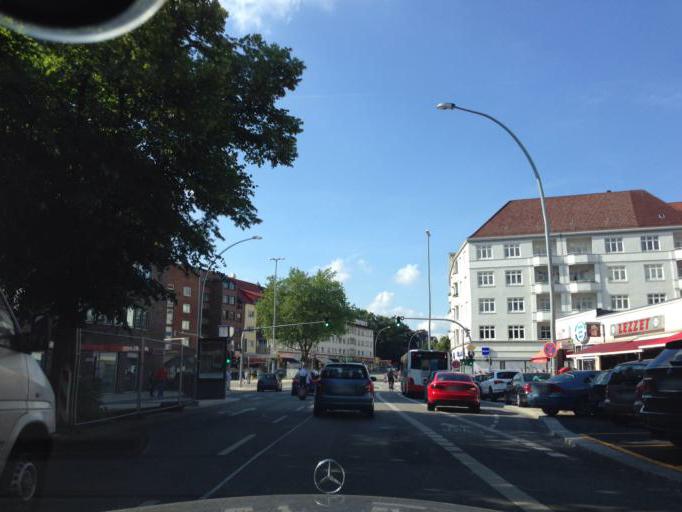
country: DE
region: Hamburg
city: Barmbek-Nord
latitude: 53.5908
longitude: 10.0447
